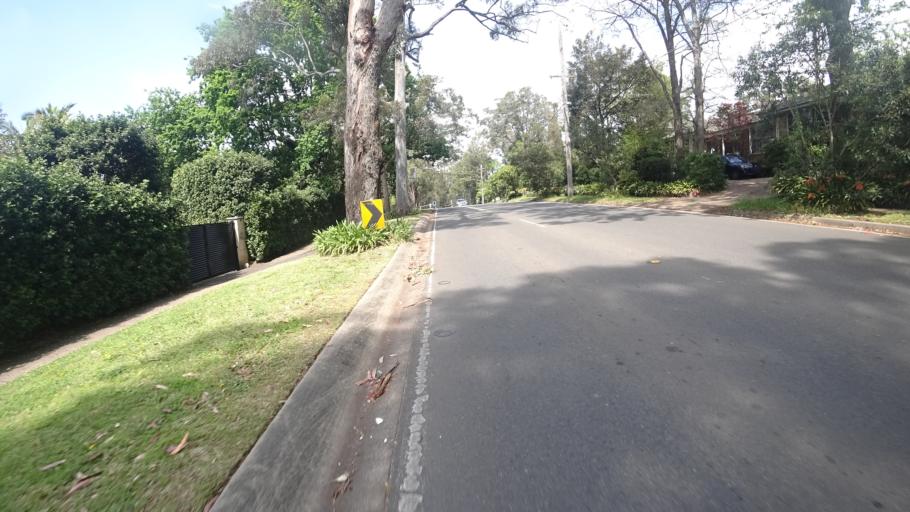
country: AU
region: New South Wales
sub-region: Ku-ring-gai
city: North Wahroonga
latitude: -33.7141
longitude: 151.1321
